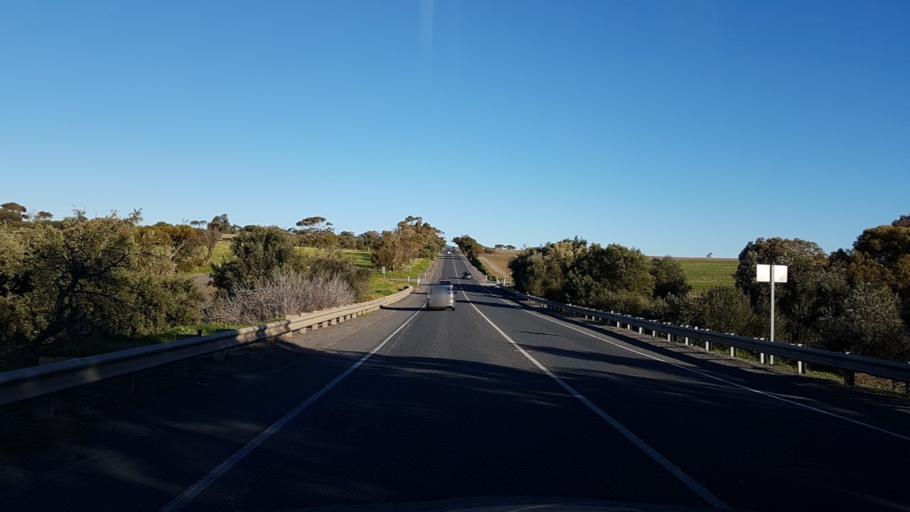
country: AU
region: South Australia
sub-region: Onkaparinga
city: Aldinga
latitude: -35.2427
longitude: 138.4939
